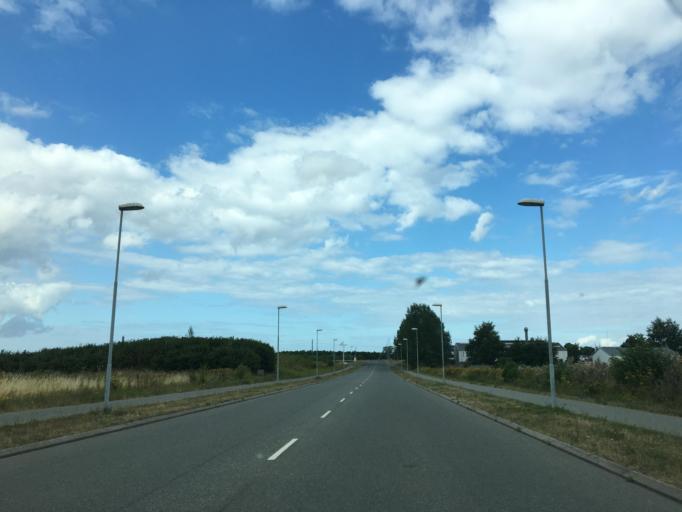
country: DK
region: South Denmark
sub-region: Nyborg Kommune
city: Nyborg
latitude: 55.3141
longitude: 10.7470
